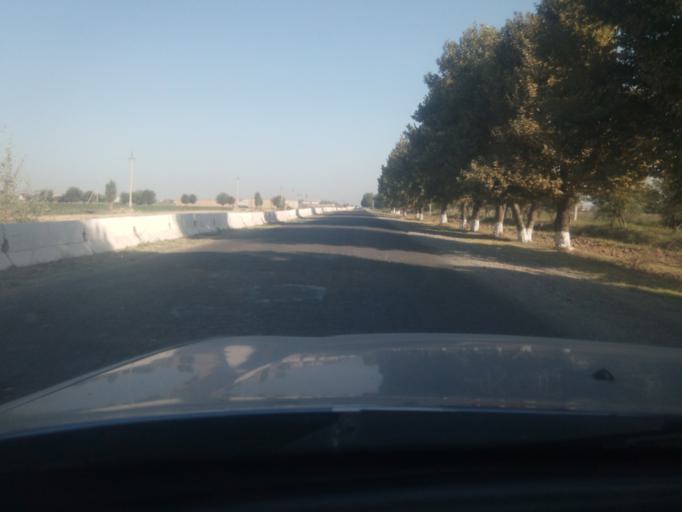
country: UZ
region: Sirdaryo
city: Guliston
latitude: 40.5029
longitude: 68.7977
